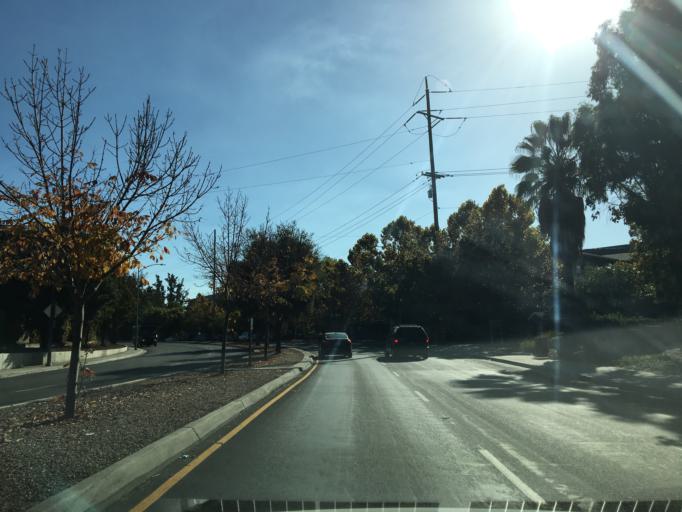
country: US
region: California
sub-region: Santa Clara County
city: San Jose
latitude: 37.3726
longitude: -121.8727
